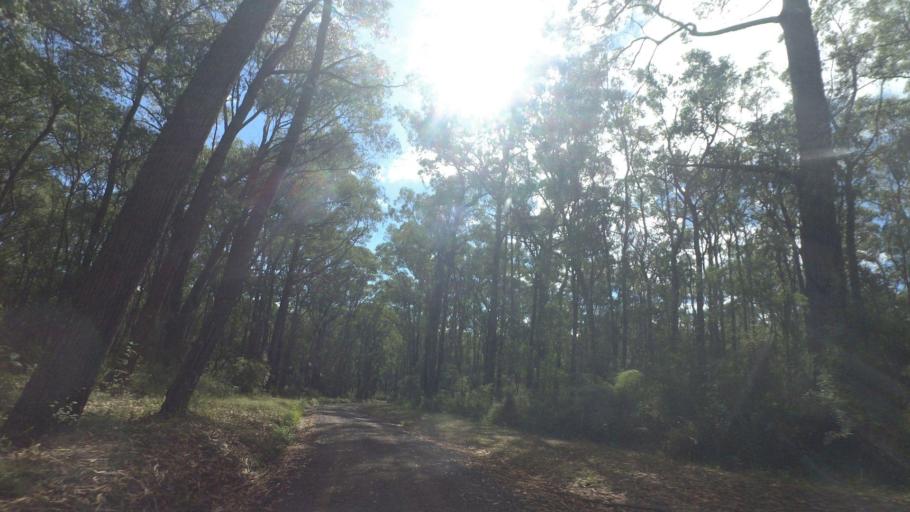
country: AU
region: Victoria
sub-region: Cardinia
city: Gembrook
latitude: -37.9096
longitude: 145.5994
